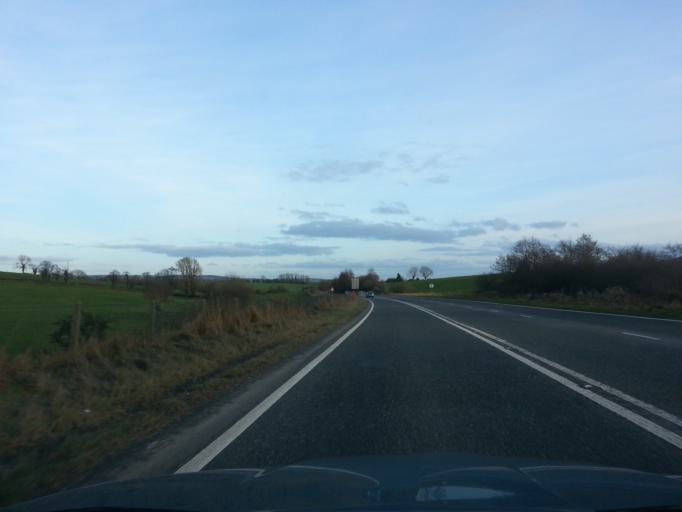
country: GB
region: Northern Ireland
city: Lisnaskea
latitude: 54.3056
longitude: -7.4892
